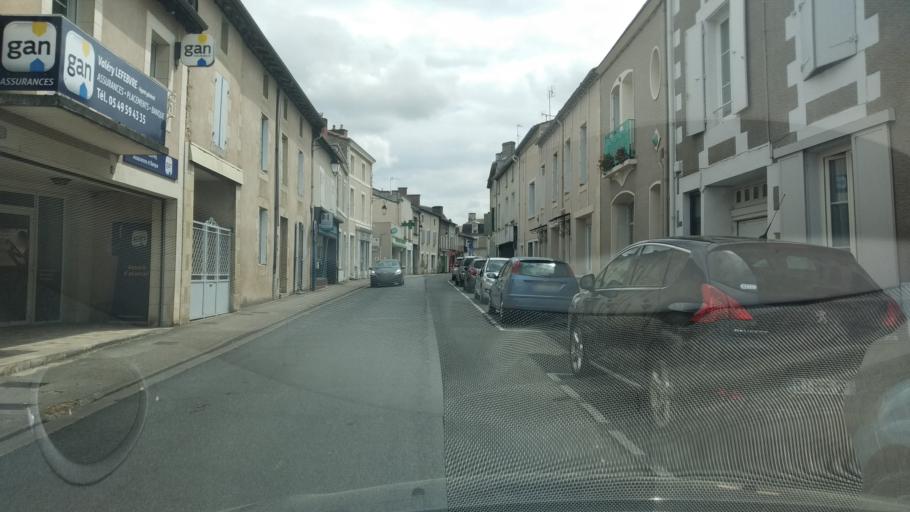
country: FR
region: Poitou-Charentes
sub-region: Departement de la Vienne
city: Saint-Maurice-la-Clouere
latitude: 46.3742
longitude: 0.4051
